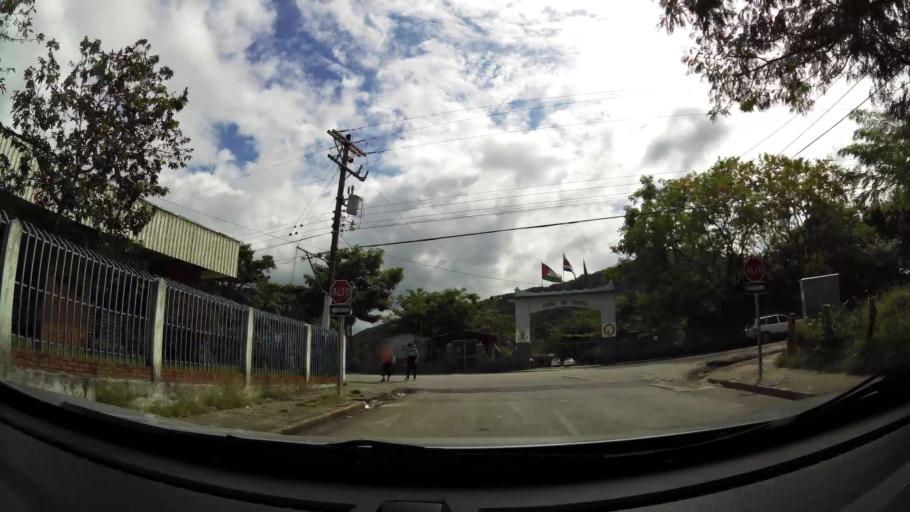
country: CR
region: Guanacaste
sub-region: Canton de Nicoya
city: Nicoya
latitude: 10.1404
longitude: -85.4522
